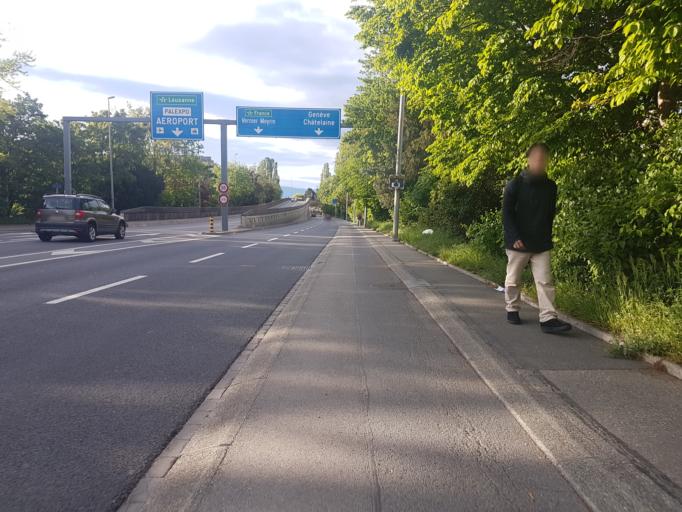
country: CH
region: Geneva
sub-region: Geneva
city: Les Avanchets
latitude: 46.2083
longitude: 6.1098
